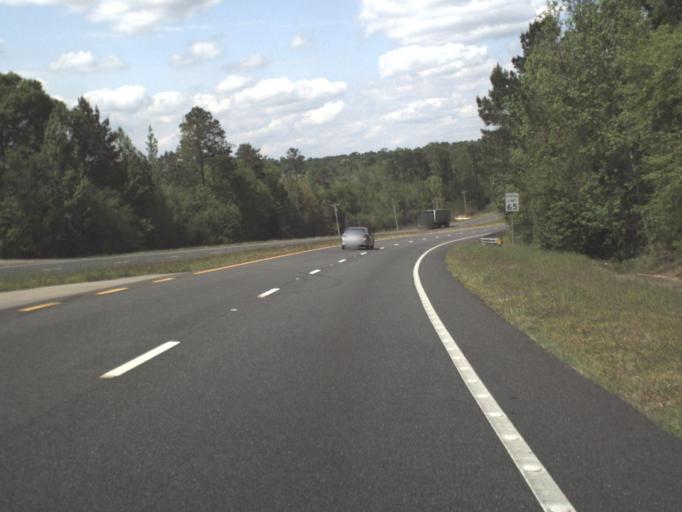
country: US
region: Florida
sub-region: Escambia County
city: Century
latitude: 30.9163
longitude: -87.3150
